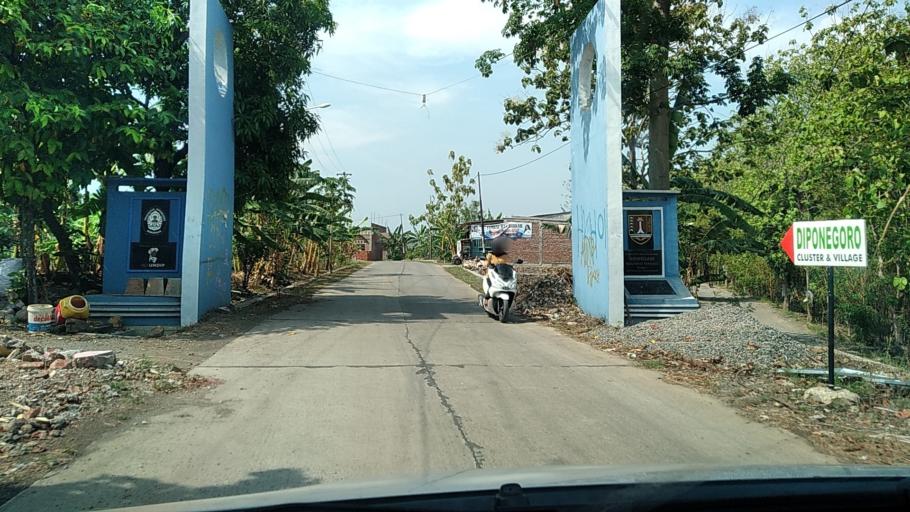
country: ID
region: Central Java
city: Mranggen
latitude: -7.0685
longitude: 110.4736
